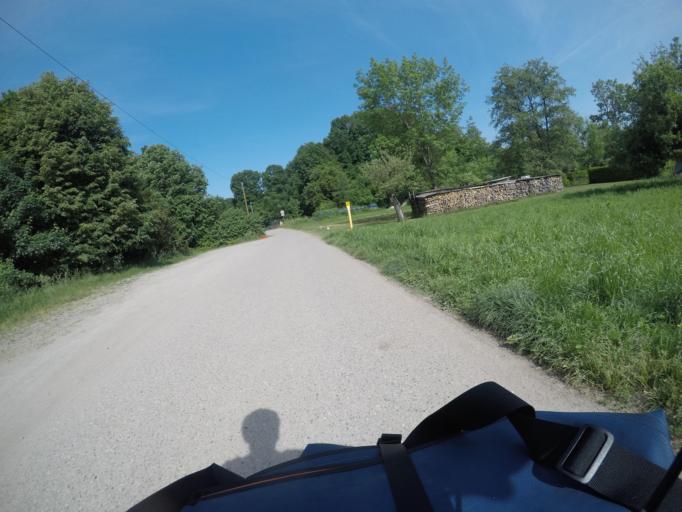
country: DE
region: Baden-Wuerttemberg
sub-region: Karlsruhe Region
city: Otigheim
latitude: 48.8956
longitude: 8.2306
